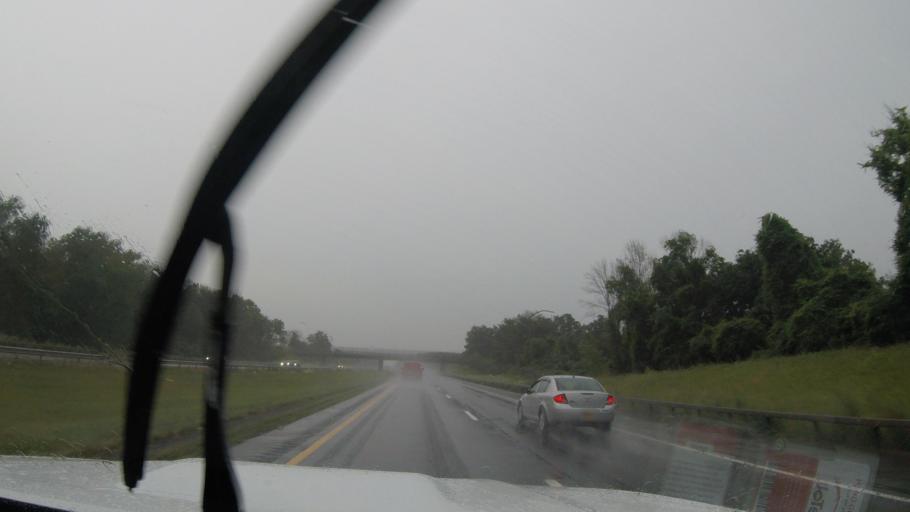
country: US
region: New York
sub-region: Seneca County
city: Seneca Falls
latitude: 42.9717
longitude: -76.8193
